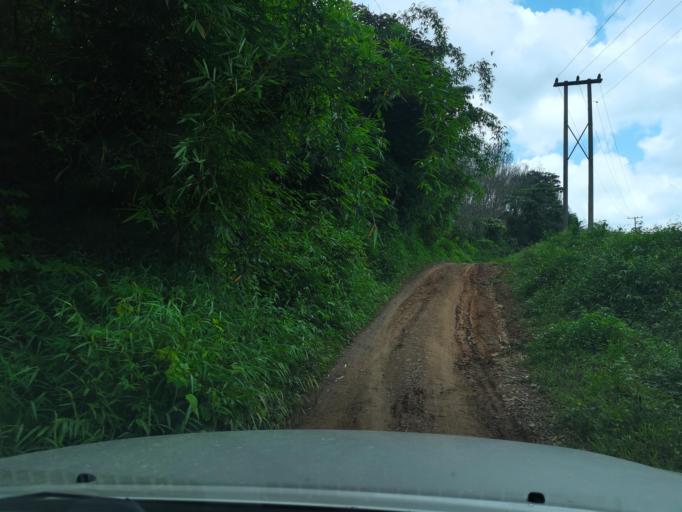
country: LA
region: Loungnamtha
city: Muang Long
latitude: 20.7547
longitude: 101.0177
